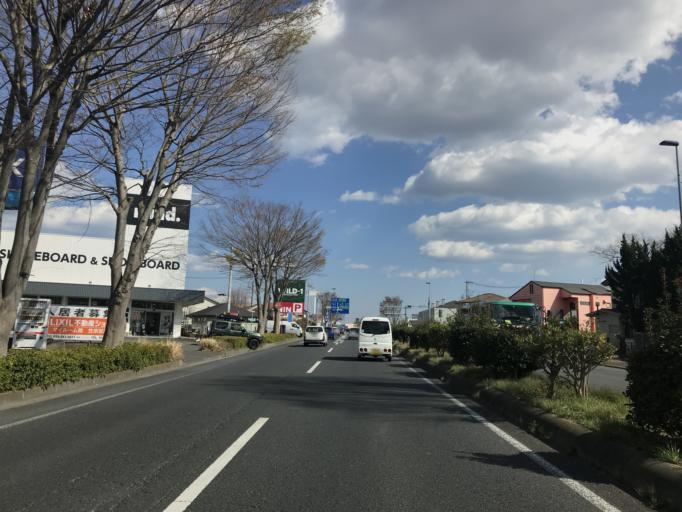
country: JP
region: Ibaraki
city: Mito-shi
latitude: 36.3432
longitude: 140.4770
